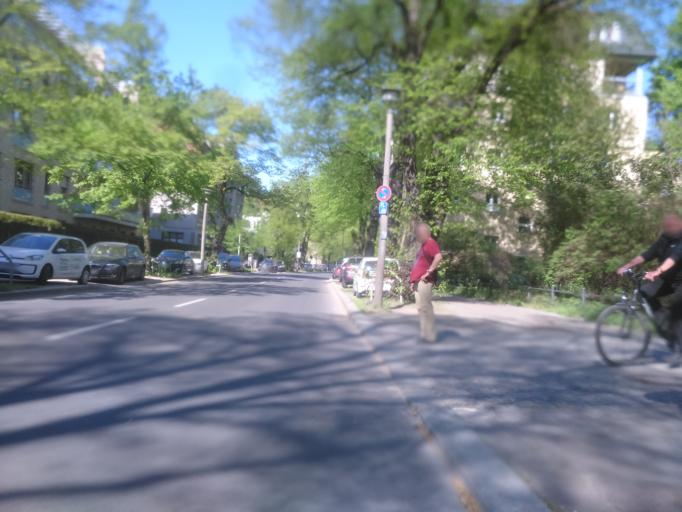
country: DE
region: Berlin
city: Weissensee
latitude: 52.5556
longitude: 13.4587
